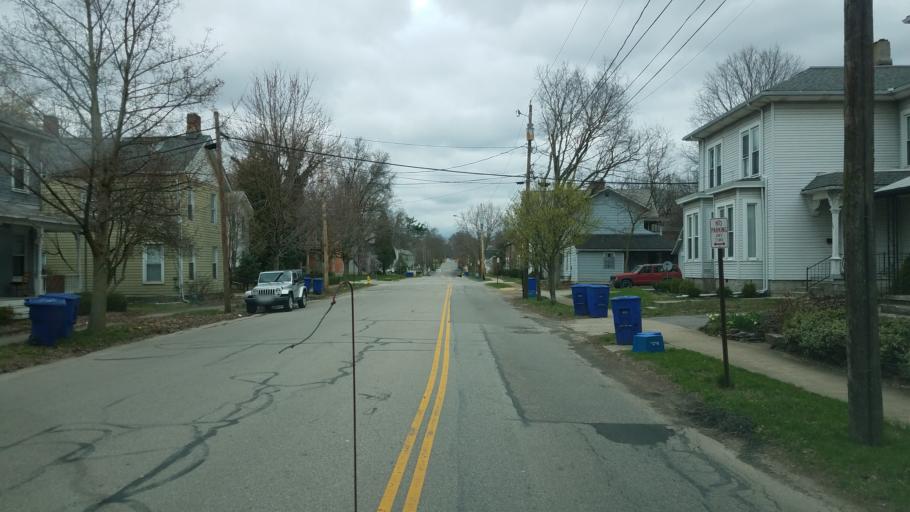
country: US
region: Ohio
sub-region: Delaware County
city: Delaware
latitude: 40.2995
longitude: -83.0730
